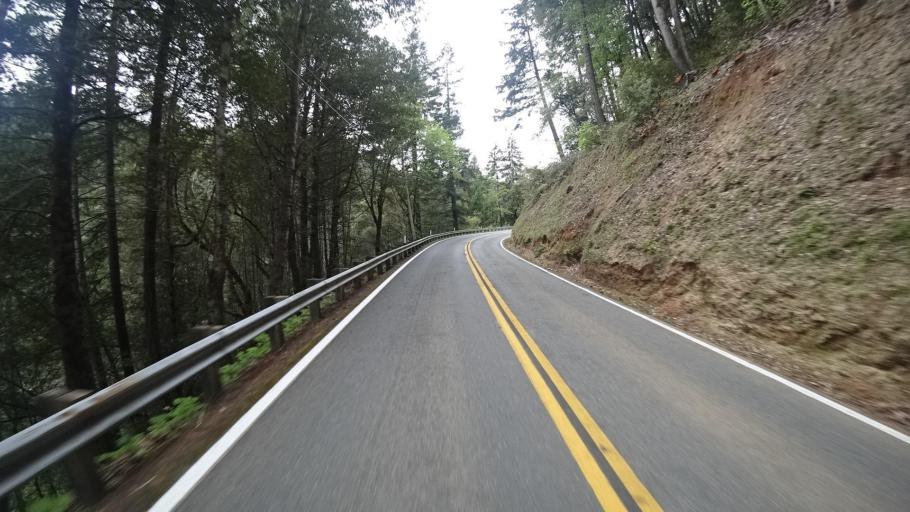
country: US
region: California
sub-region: Humboldt County
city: Willow Creek
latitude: 41.0104
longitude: -123.6373
